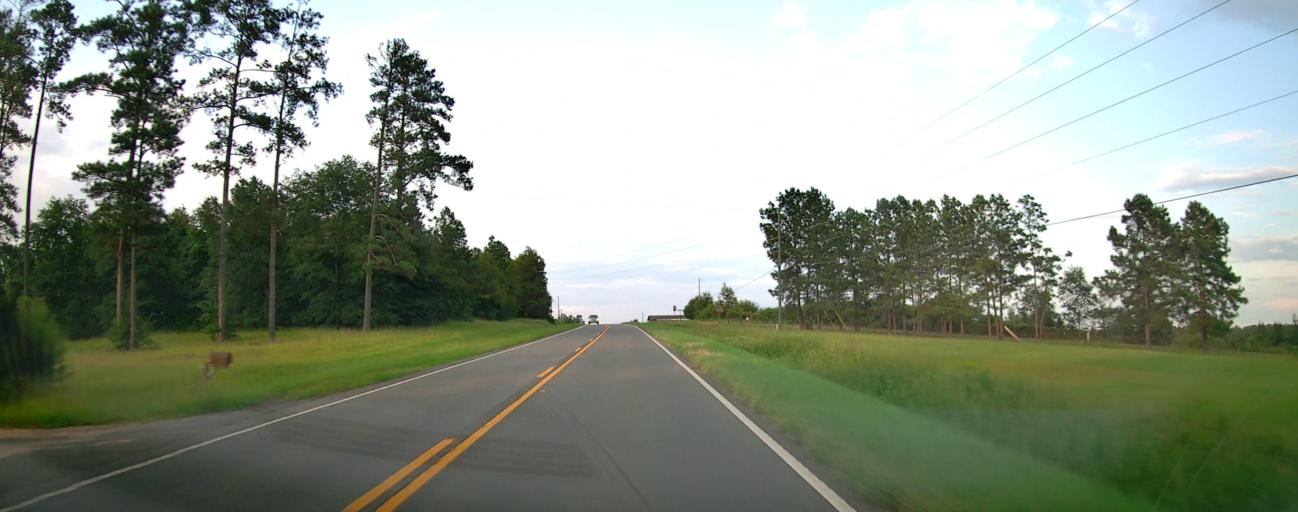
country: US
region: Georgia
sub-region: Crawford County
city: Roberta
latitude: 32.6739
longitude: -84.0916
